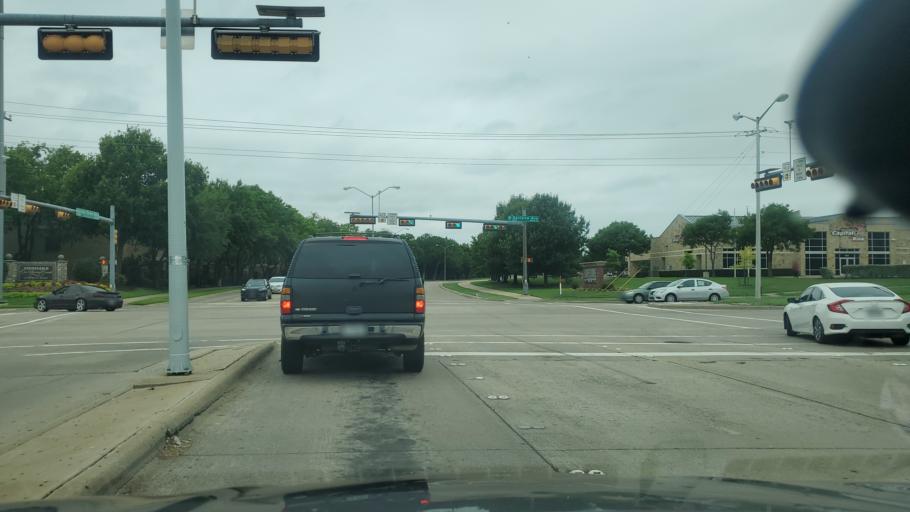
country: US
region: Texas
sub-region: Dallas County
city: Garland
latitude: 32.9611
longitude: -96.6472
